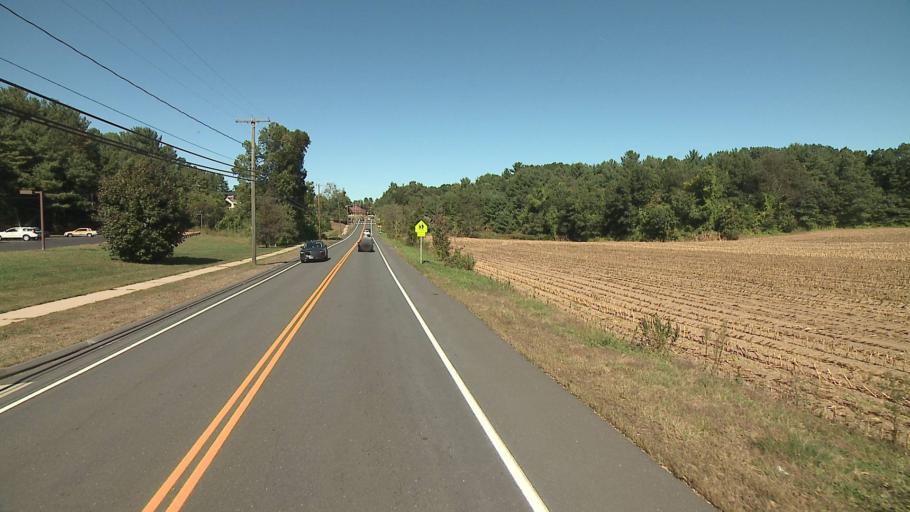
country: US
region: Connecticut
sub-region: Hartford County
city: Salmon Brook
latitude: 41.9572
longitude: -72.7903
